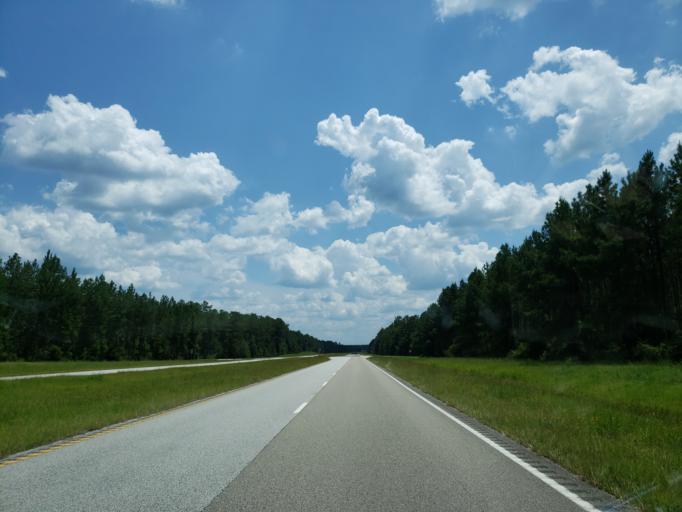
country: US
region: Mississippi
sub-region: Greene County
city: Leakesville
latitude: 31.1676
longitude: -88.5016
